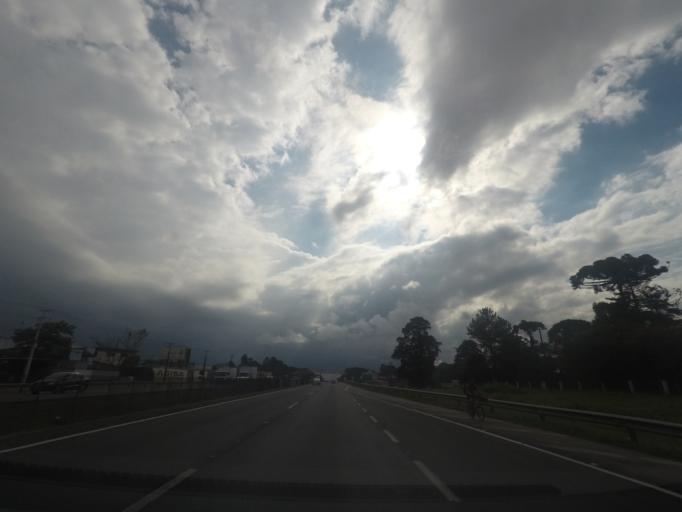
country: BR
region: Parana
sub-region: Sao Jose Dos Pinhais
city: Sao Jose dos Pinhais
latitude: -25.5094
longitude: -49.1327
